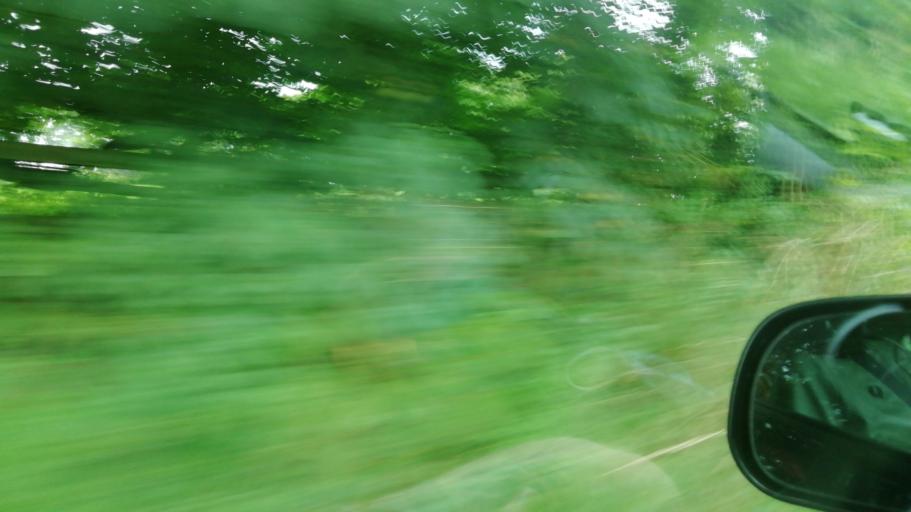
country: IE
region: Munster
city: Fethard
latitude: 52.5769
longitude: -7.5854
